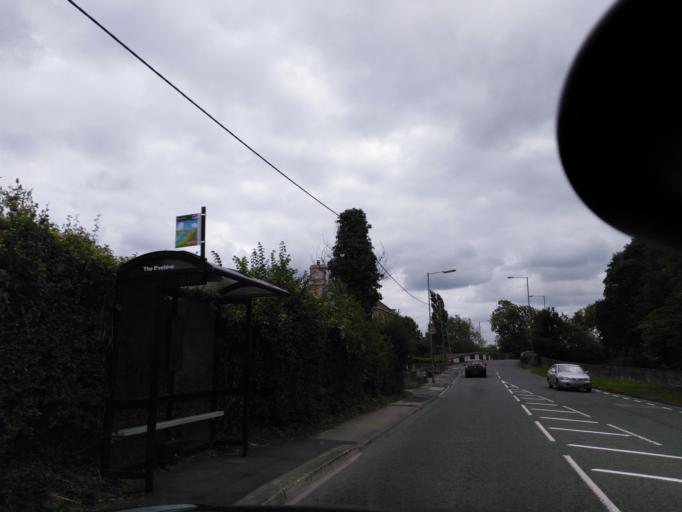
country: GB
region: England
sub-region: Wiltshire
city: Bradford-on-Avon
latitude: 51.3368
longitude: -2.2402
